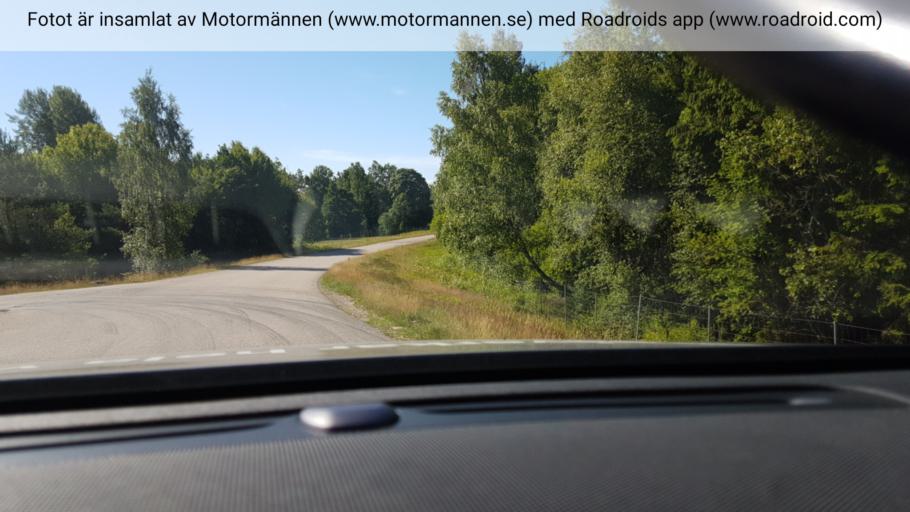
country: SE
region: Kronoberg
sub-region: Markaryds Kommun
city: Stromsnasbruk
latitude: 56.6150
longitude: 13.7613
